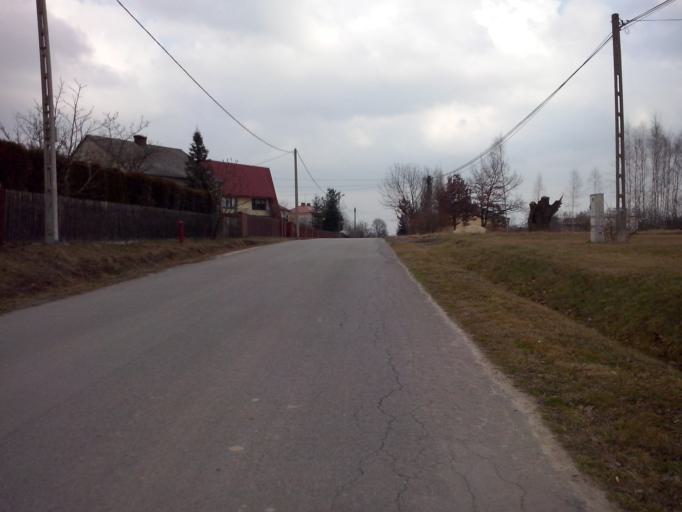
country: PL
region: Subcarpathian Voivodeship
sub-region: Powiat nizanski
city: Krzeszow
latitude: 50.4271
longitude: 22.3422
